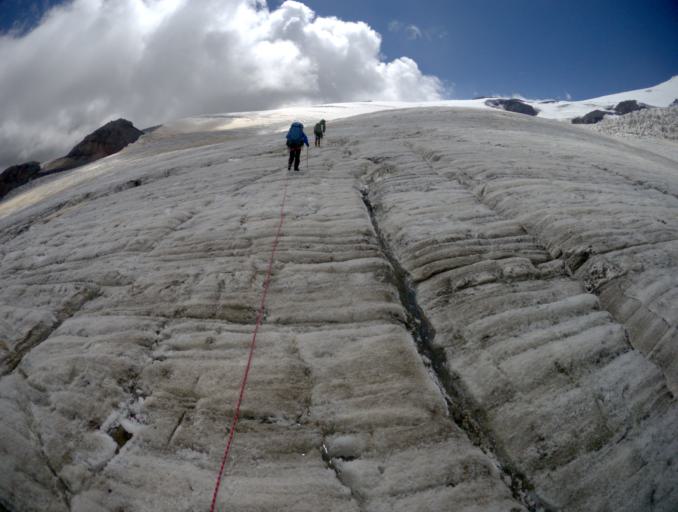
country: RU
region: Kabardino-Balkariya
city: Terskol
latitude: 43.3273
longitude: 42.5107
